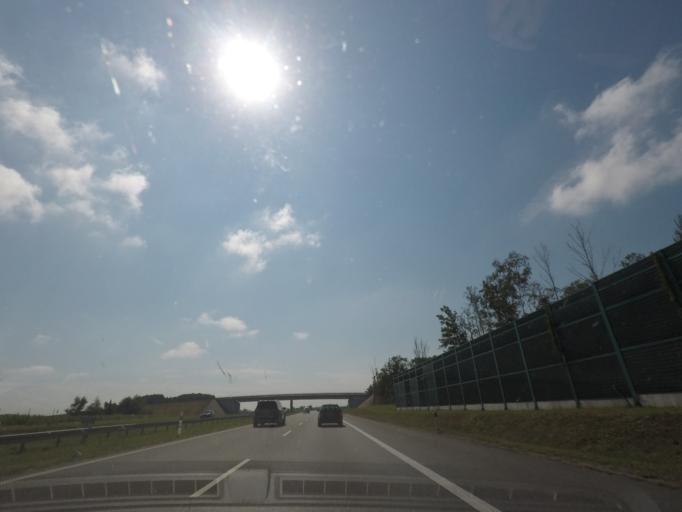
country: PL
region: Lodz Voivodeship
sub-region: Powiat kutnowski
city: Lanieta
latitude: 52.4139
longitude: 19.2647
